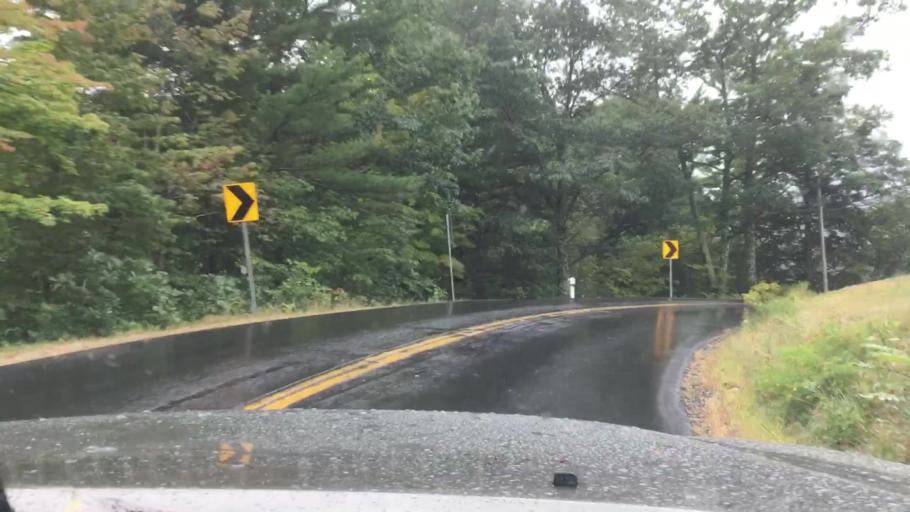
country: US
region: New Hampshire
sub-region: Belknap County
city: Meredith
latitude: 43.6836
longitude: -71.5205
